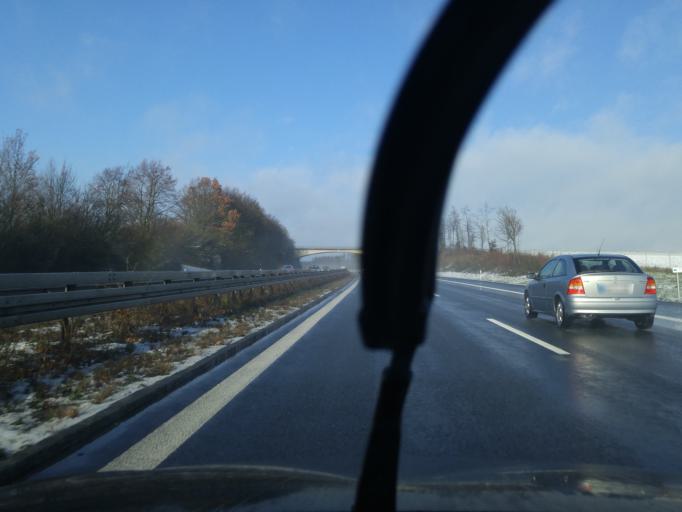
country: DE
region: Bavaria
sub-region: Regierungsbezirk Unterfranken
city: Werneck
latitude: 50.0375
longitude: 10.0685
